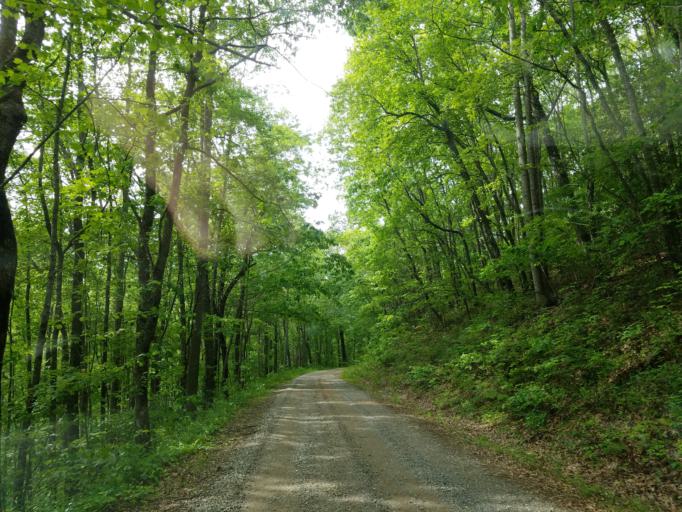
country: US
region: Georgia
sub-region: Union County
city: Blairsville
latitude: 34.7455
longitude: -83.9926
